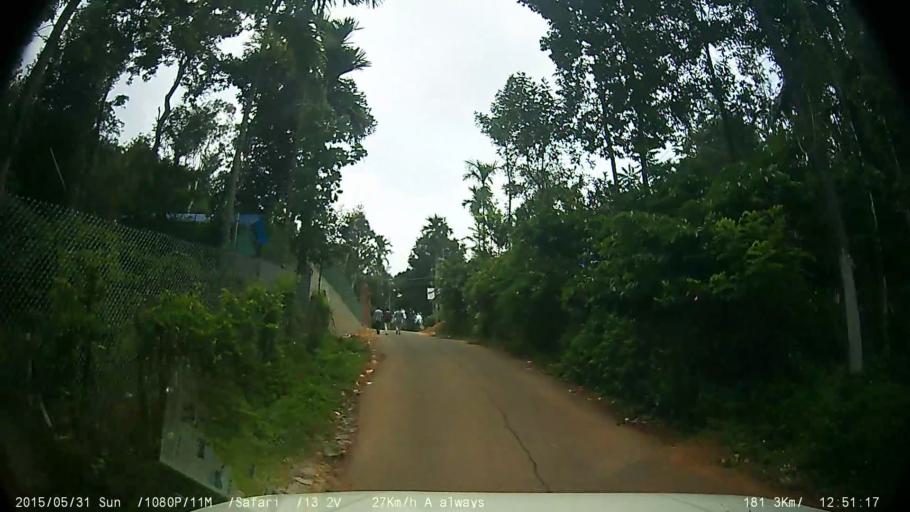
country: IN
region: Kerala
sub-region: Wayanad
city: Kalpetta
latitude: 11.5088
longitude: 76.1542
